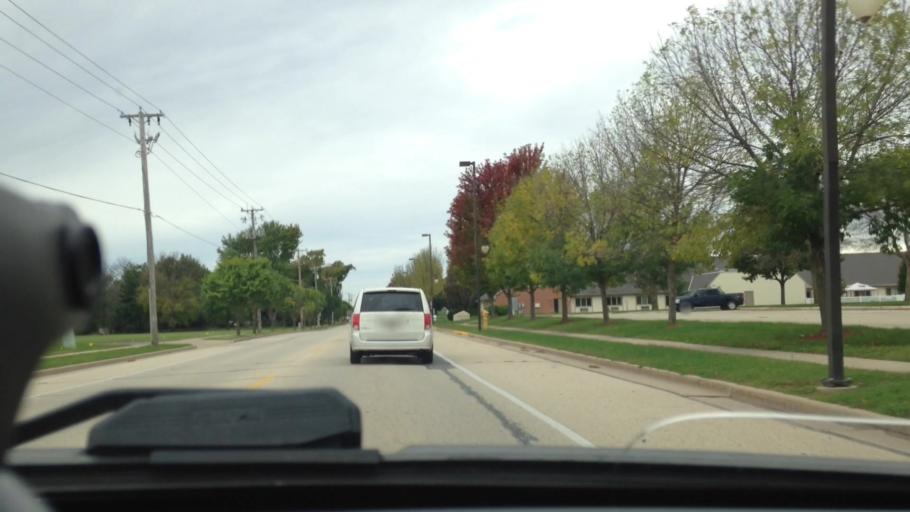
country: US
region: Wisconsin
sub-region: Fond du Lac County
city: North Fond du Lac
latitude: 43.8065
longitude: -88.4879
